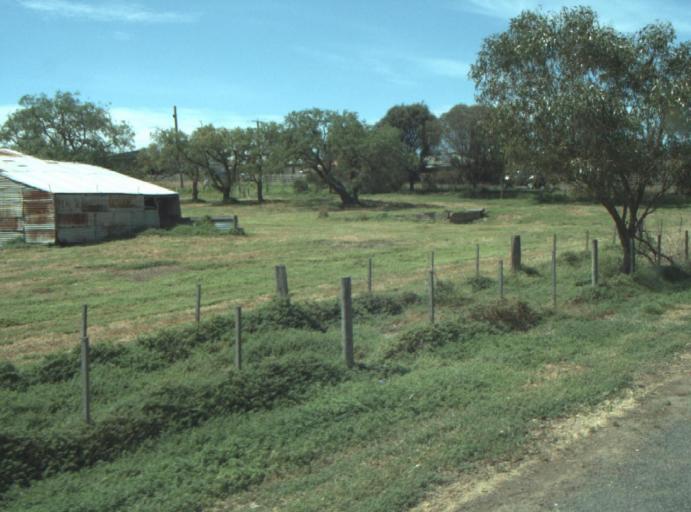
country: AU
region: Victoria
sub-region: Greater Geelong
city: Leopold
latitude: -38.1750
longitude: 144.4711
